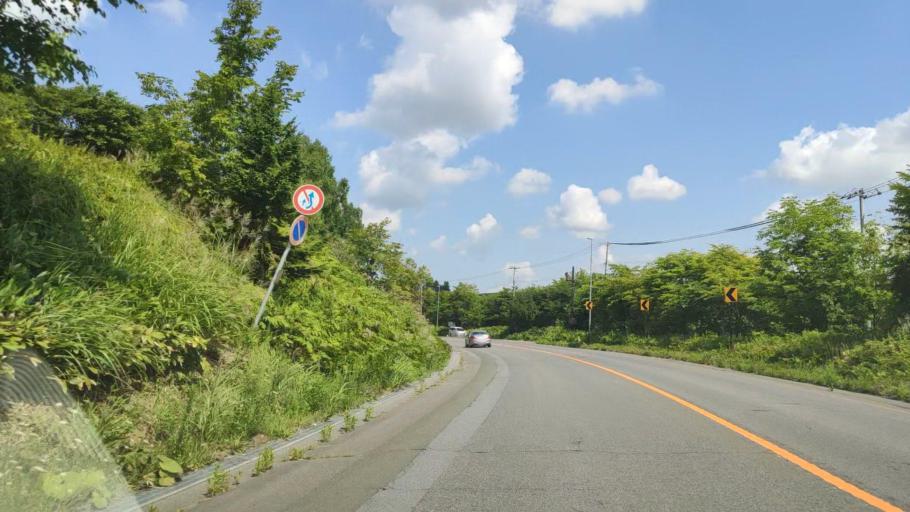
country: JP
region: Hokkaido
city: Shimo-furano
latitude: 43.5508
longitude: 142.4393
